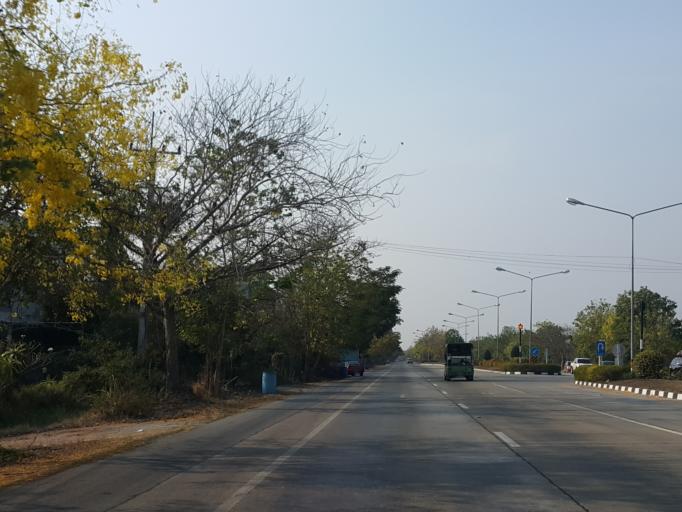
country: TH
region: Suphan Buri
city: Sam Chuk
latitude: 14.7710
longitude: 100.0916
